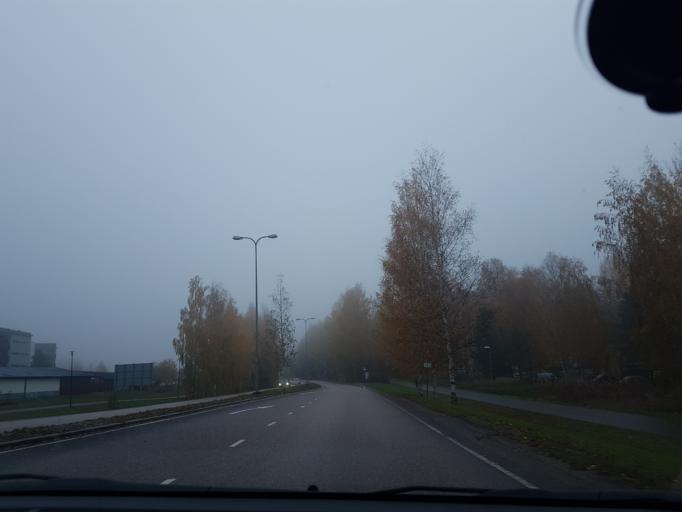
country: FI
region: Uusimaa
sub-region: Helsinki
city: Tuusula
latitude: 60.4036
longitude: 25.0338
